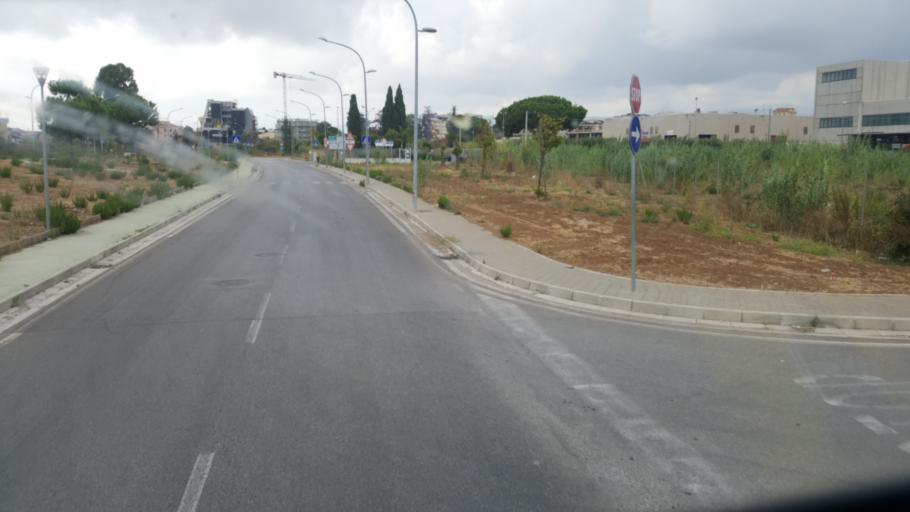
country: IT
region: Campania
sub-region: Provincia di Salerno
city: Battipaglia
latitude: 40.6012
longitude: 14.9853
